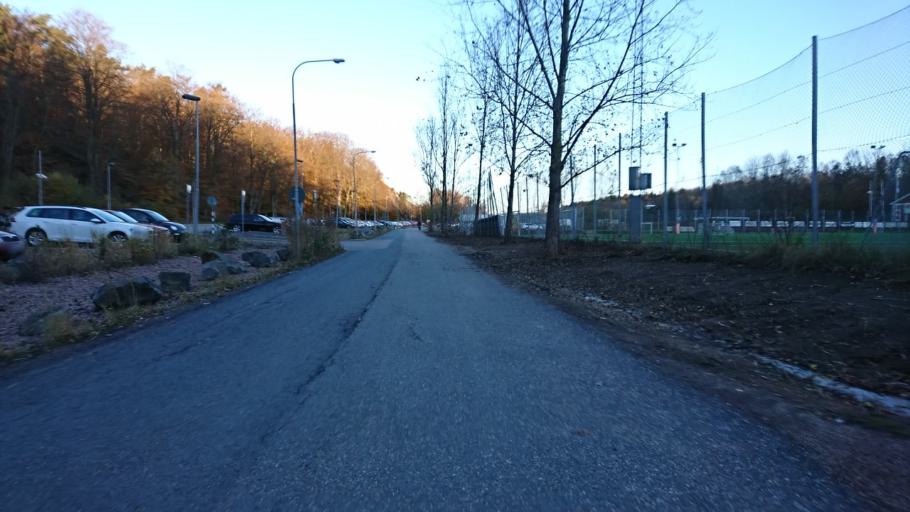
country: SE
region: Vaestra Goetaland
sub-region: Molndal
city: Moelndal
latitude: 57.6737
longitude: 12.0265
